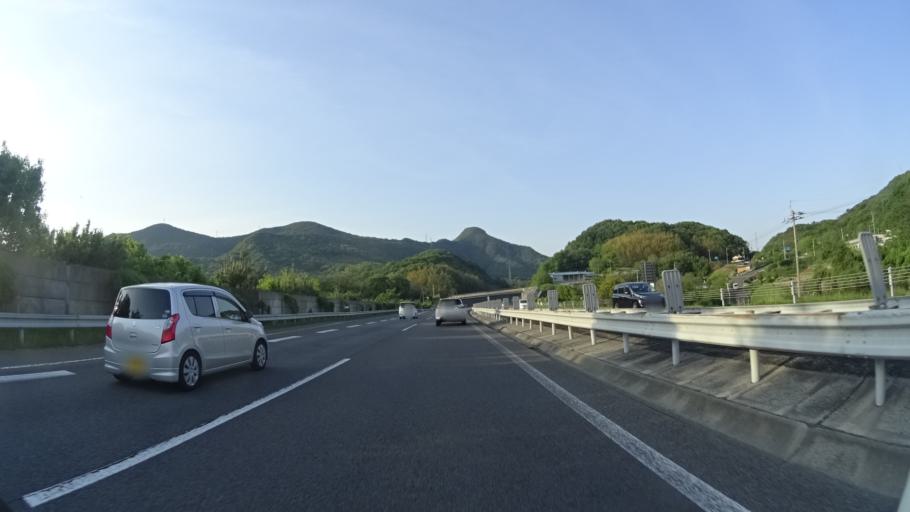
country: JP
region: Kagawa
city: Tadotsu
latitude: 34.2178
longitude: 133.7288
